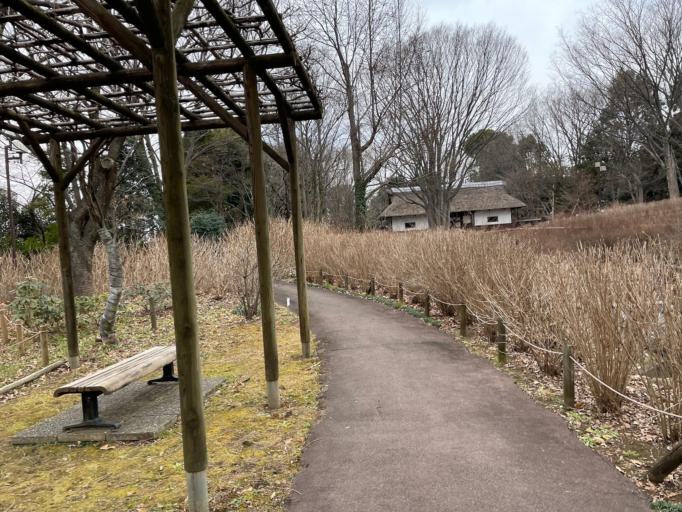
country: JP
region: Tokyo
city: Kokubunji
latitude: 35.6551
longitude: 139.4711
